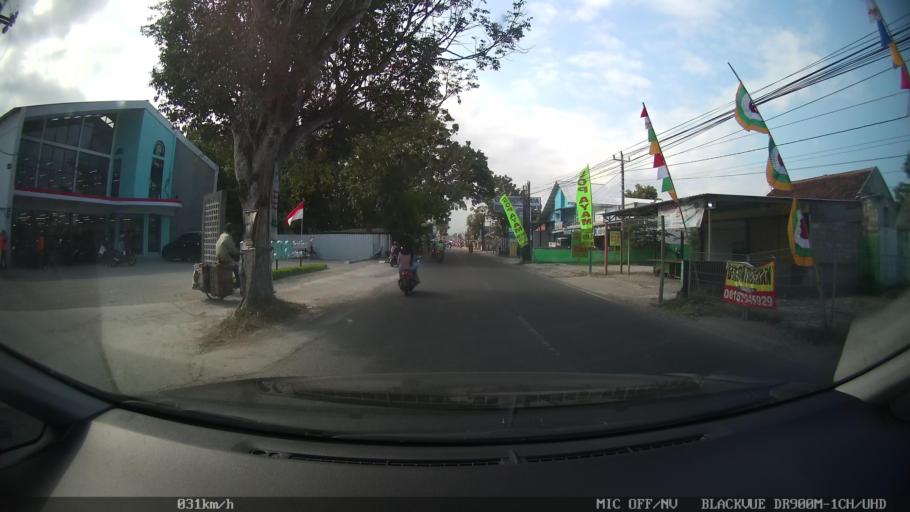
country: ID
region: Daerah Istimewa Yogyakarta
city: Sewon
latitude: -7.8483
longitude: 110.3907
